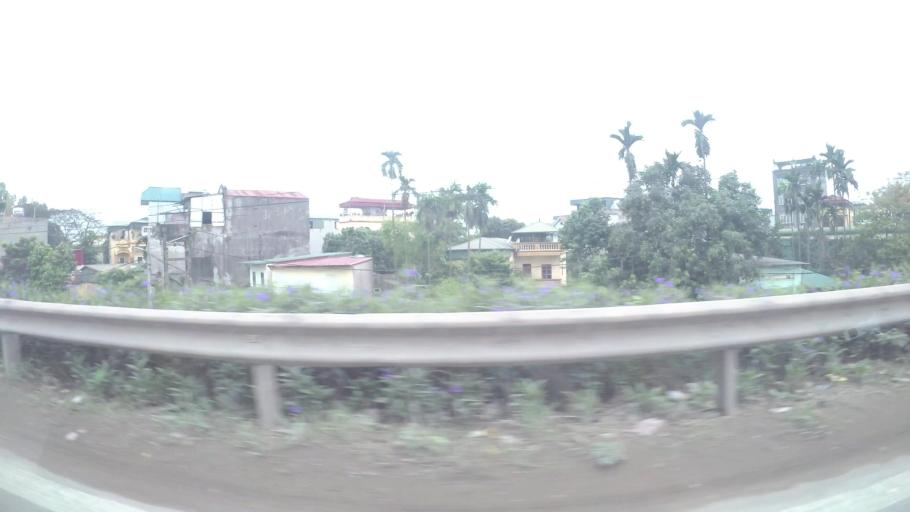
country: VN
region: Ha Noi
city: Hai BaTrung
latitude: 20.9910
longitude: 105.8930
